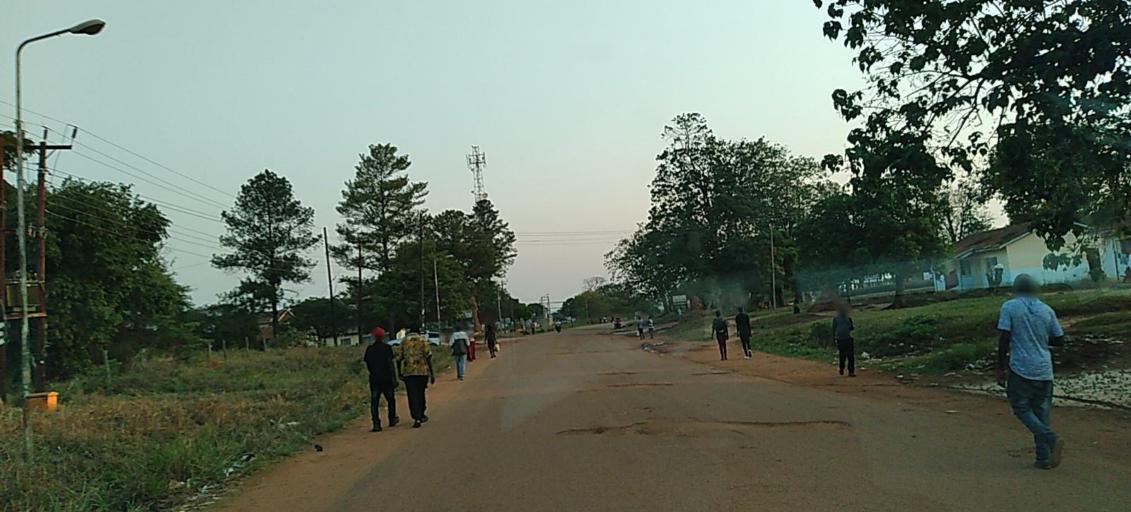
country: ZM
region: North-Western
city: Mwinilunga
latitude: -11.7374
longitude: 24.4309
